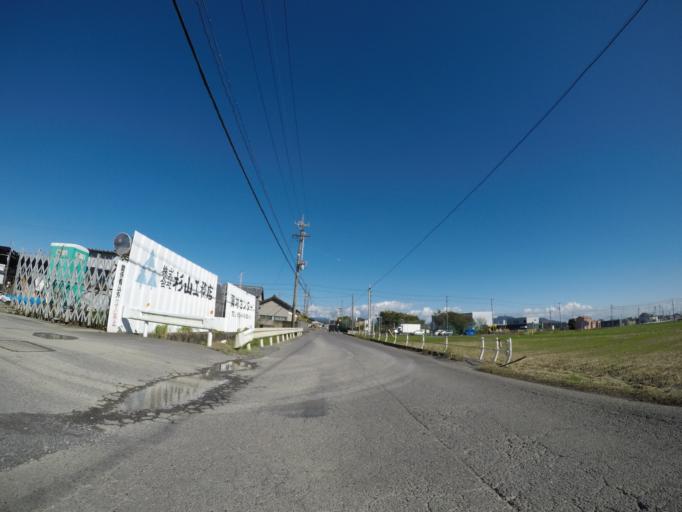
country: JP
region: Shizuoka
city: Fujieda
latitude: 34.8370
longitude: 138.2394
